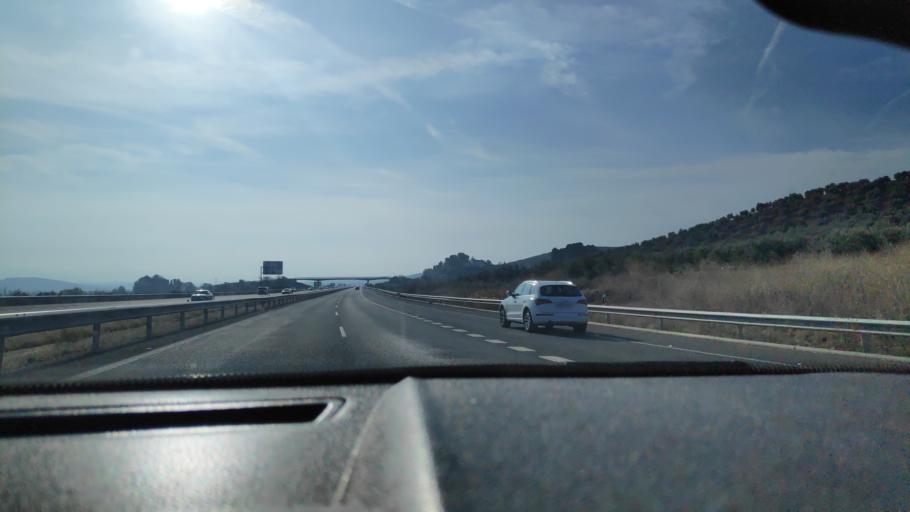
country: ES
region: Andalusia
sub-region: Provincia de Jaen
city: Mengibar
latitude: 37.9061
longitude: -3.7834
